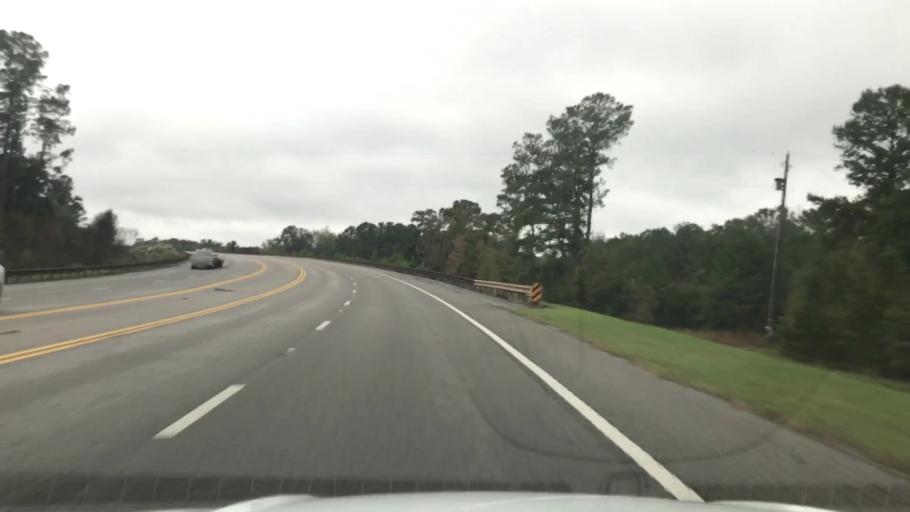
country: US
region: South Carolina
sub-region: Colleton County
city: Walterboro
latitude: 32.7366
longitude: -80.5897
